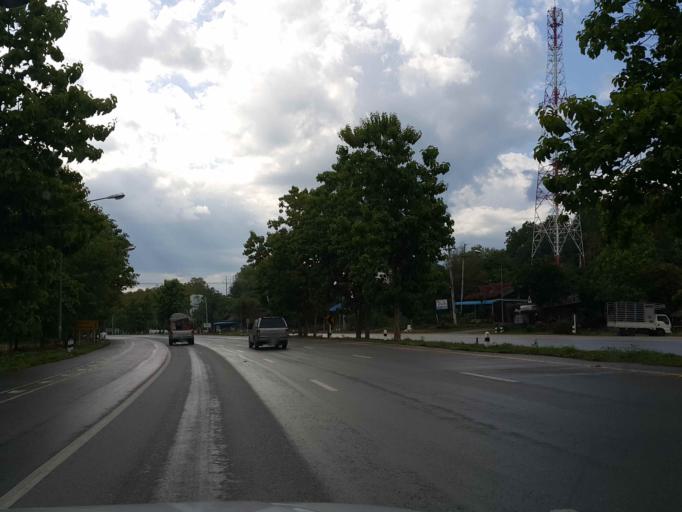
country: TH
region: Lampang
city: Thoen
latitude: 17.6580
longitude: 99.2501
